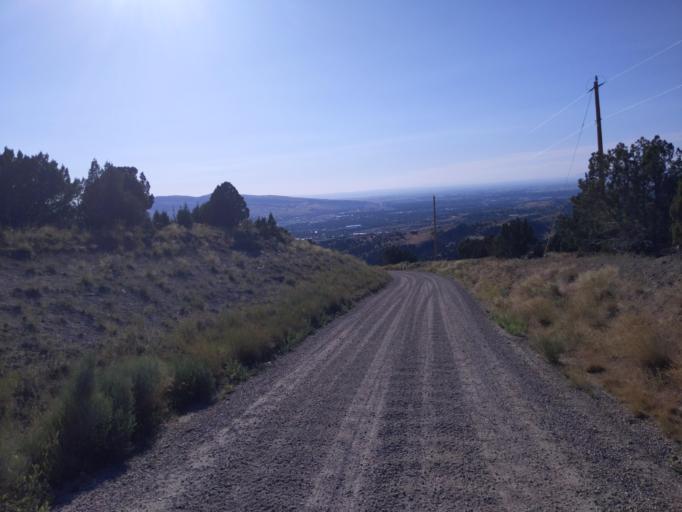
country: US
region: Idaho
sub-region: Bannock County
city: Pocatello
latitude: 42.8534
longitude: -112.3826
